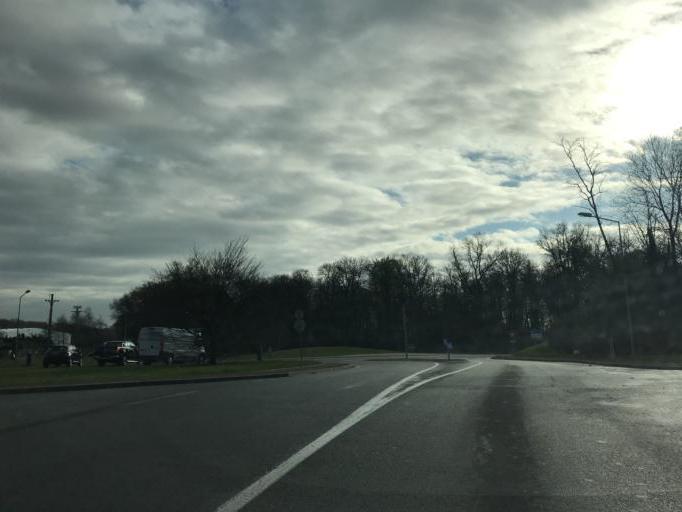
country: FR
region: Rhone-Alpes
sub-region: Departement de l'Ain
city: Reyrieux
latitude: 45.9427
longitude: 4.8167
